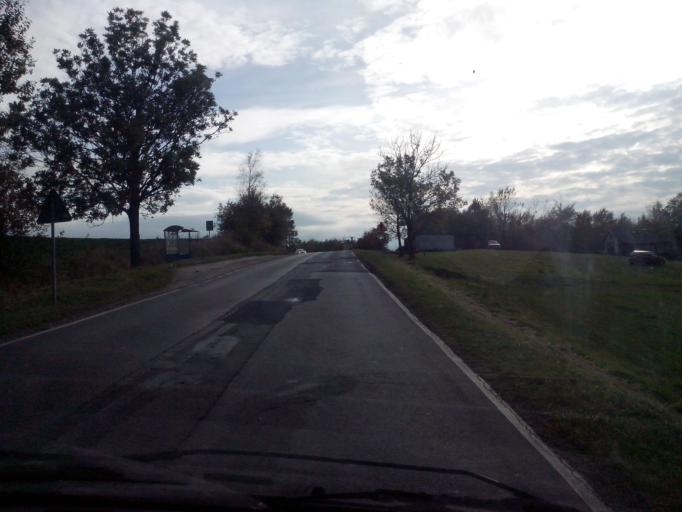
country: PL
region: Subcarpathian Voivodeship
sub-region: Powiat ropczycko-sedziszowski
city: Wielopole Skrzynskie
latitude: 49.9167
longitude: 21.6148
